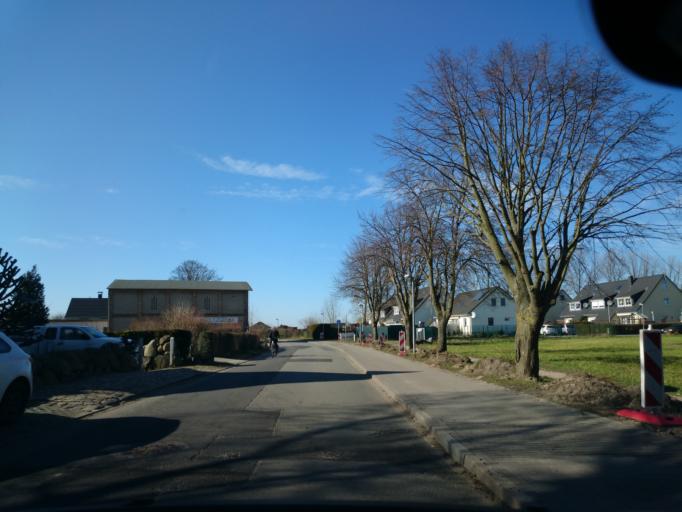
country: DE
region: Mecklenburg-Vorpommern
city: Borgerende-Rethwisch
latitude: 54.1419
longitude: 11.9327
